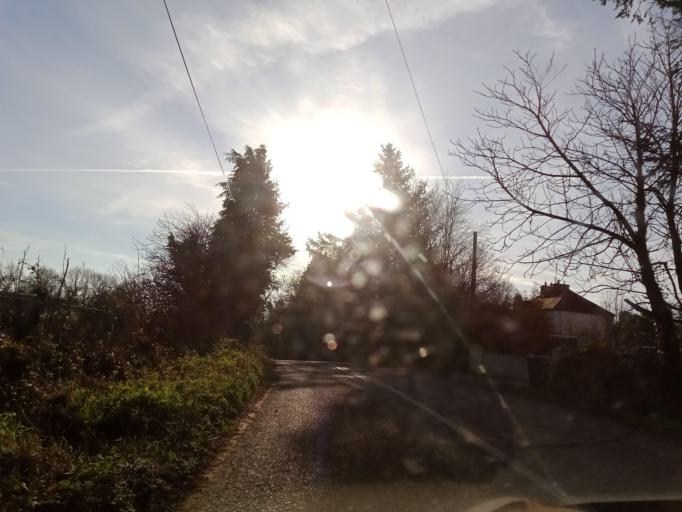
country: IE
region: Munster
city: Fethard
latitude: 52.5809
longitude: -7.5686
